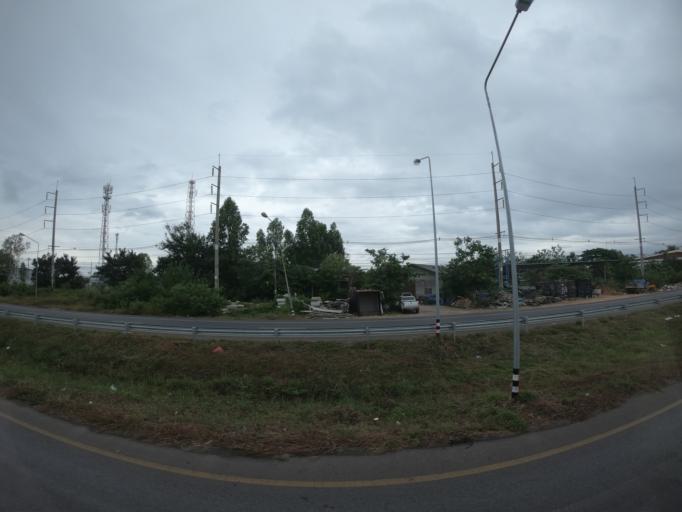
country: TH
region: Roi Et
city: Roi Et
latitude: 16.0469
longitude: 103.6226
